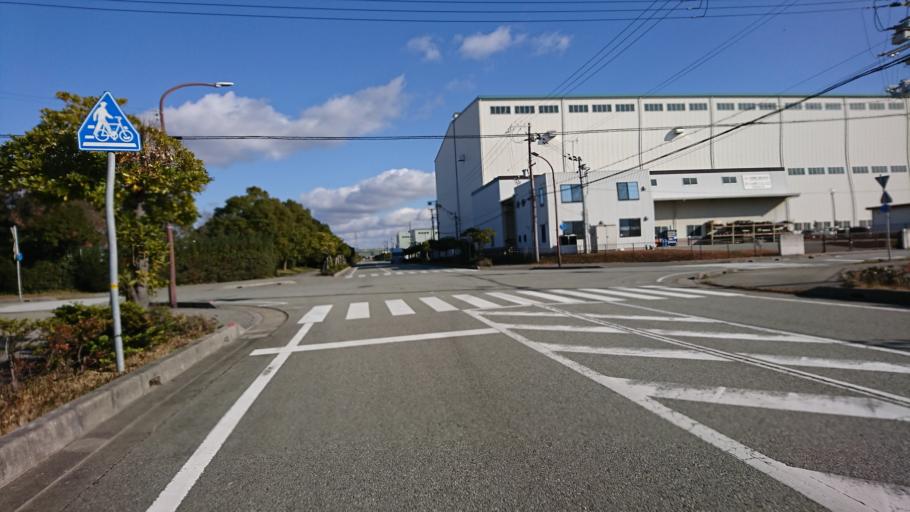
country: JP
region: Hyogo
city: Kakogawacho-honmachi
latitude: 34.7525
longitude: 134.7839
